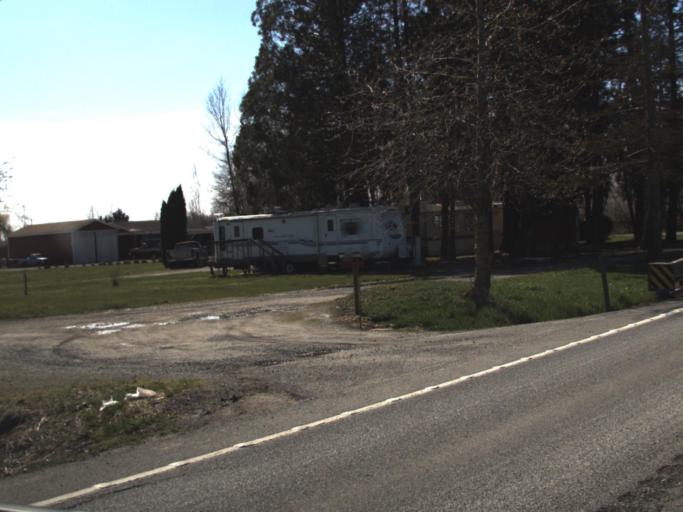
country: US
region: Washington
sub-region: Pierce County
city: Buckley
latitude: 47.2101
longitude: -122.0617
